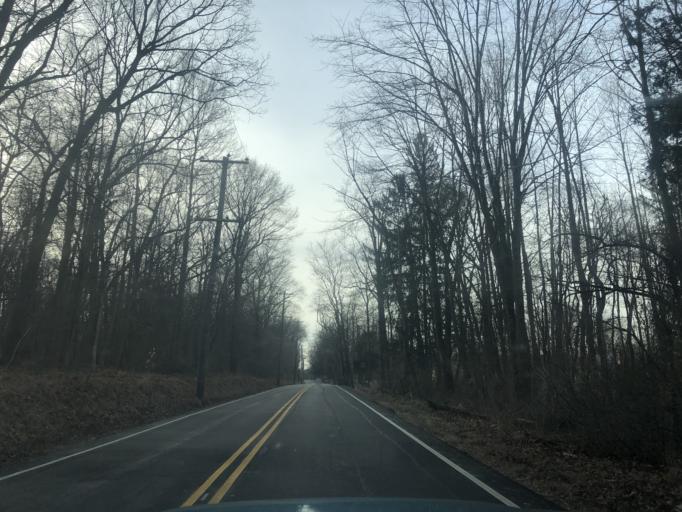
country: US
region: Pennsylvania
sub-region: Montgomery County
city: Flourtown
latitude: 40.1216
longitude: -75.2368
